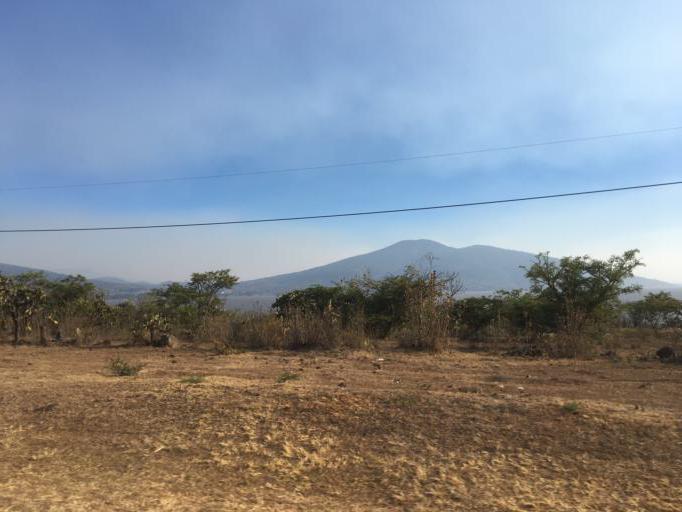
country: MX
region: Michoacan
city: Santa Fe de la Laguna
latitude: 19.6720
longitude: -101.5733
